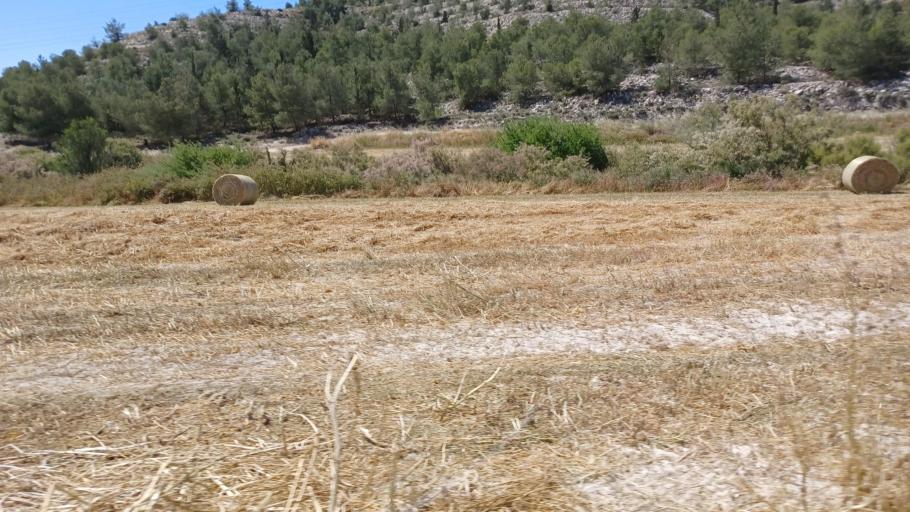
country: CY
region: Lefkosia
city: Lympia
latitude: 34.9942
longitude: 33.5256
